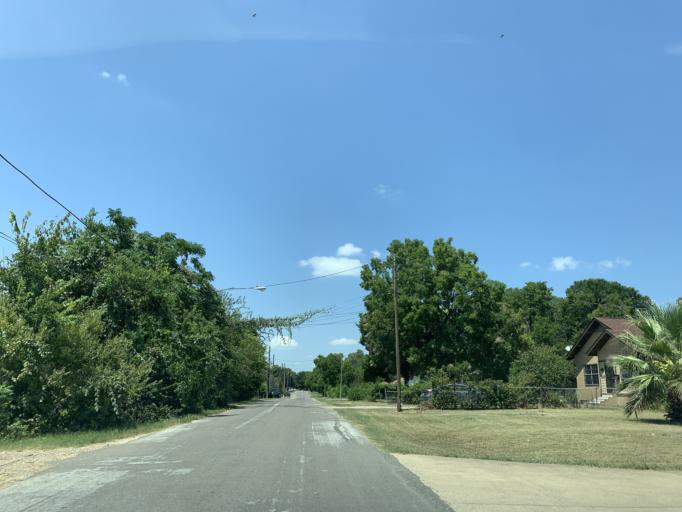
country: US
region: Texas
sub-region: Dallas County
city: Hutchins
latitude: 32.6863
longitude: -96.7755
